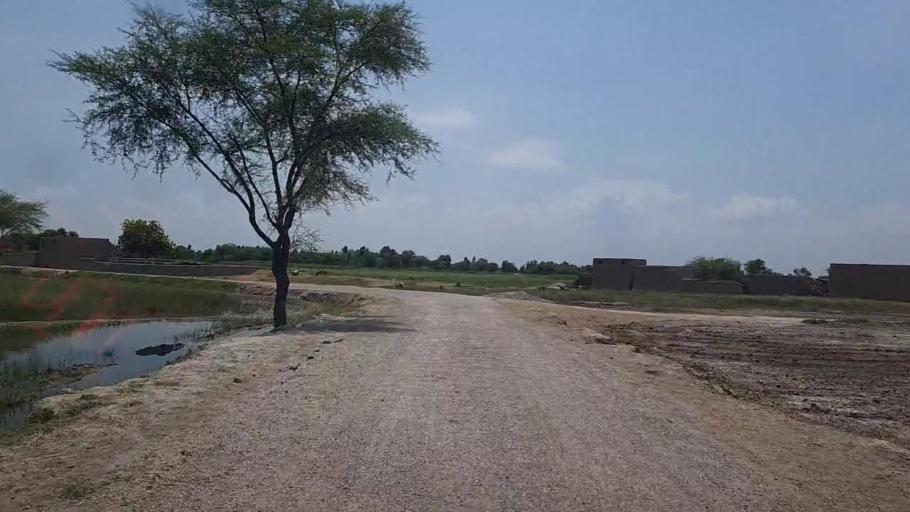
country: PK
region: Sindh
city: Ubauro
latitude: 28.1533
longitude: 69.7662
